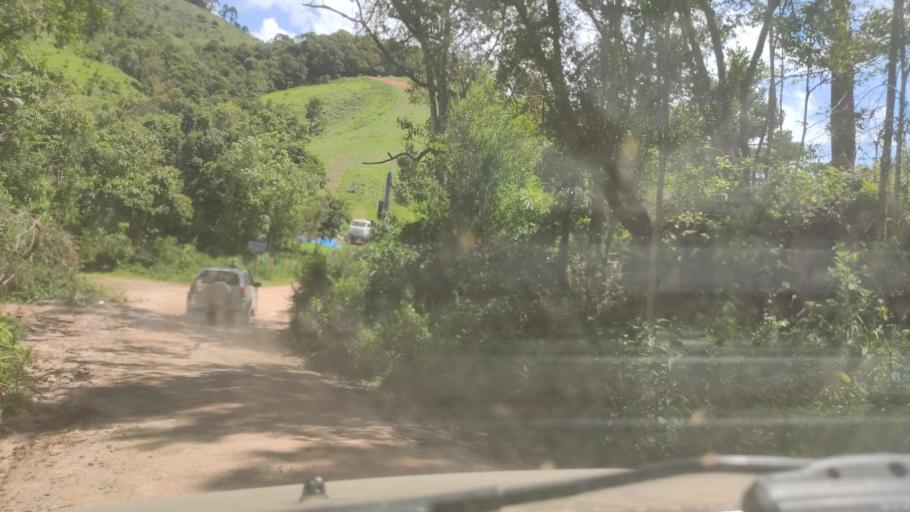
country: BR
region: Minas Gerais
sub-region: Cambui
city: Cambui
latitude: -22.6860
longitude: -45.9752
